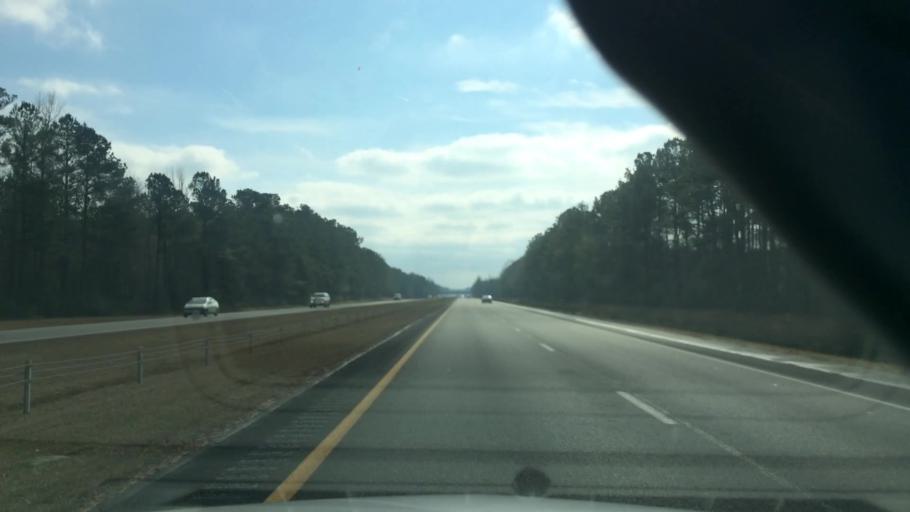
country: US
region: North Carolina
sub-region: Pender County
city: Rocky Point
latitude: 34.4921
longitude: -77.8776
